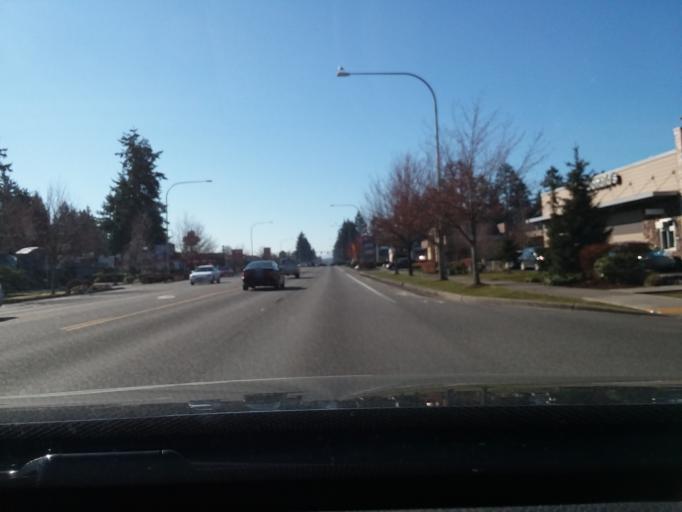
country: US
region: Washington
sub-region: Pierce County
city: Spanaway
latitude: 47.1217
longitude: -122.4350
